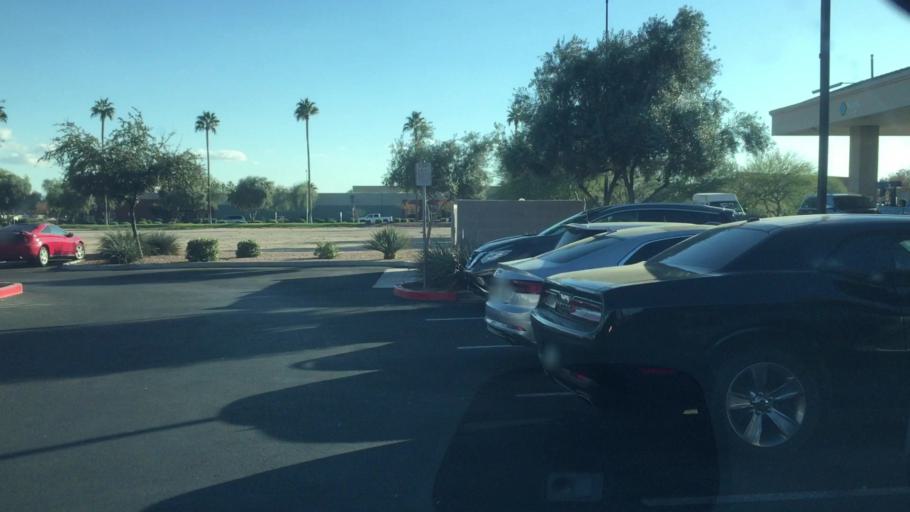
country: US
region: Arizona
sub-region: Maricopa County
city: Guadalupe
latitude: 33.3140
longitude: -111.9684
